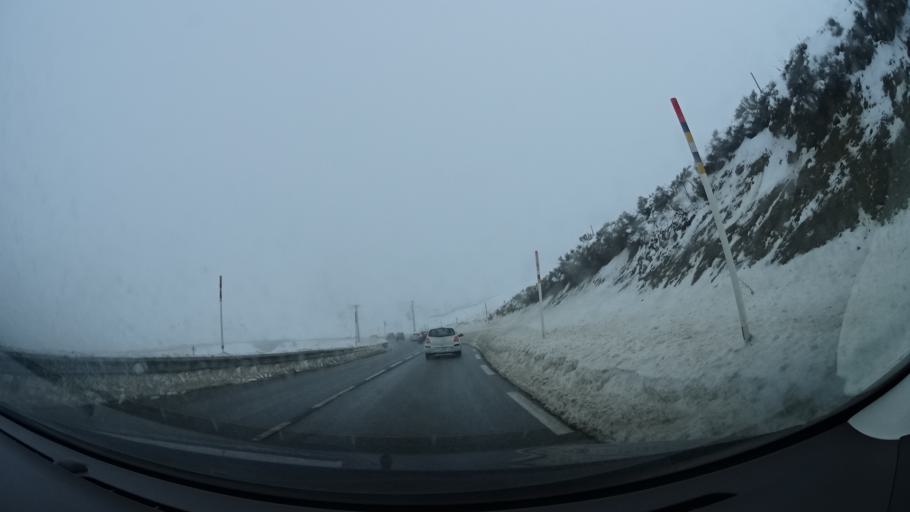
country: AD
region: Encamp
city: Pas de la Casa
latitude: 42.5586
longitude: 1.7671
